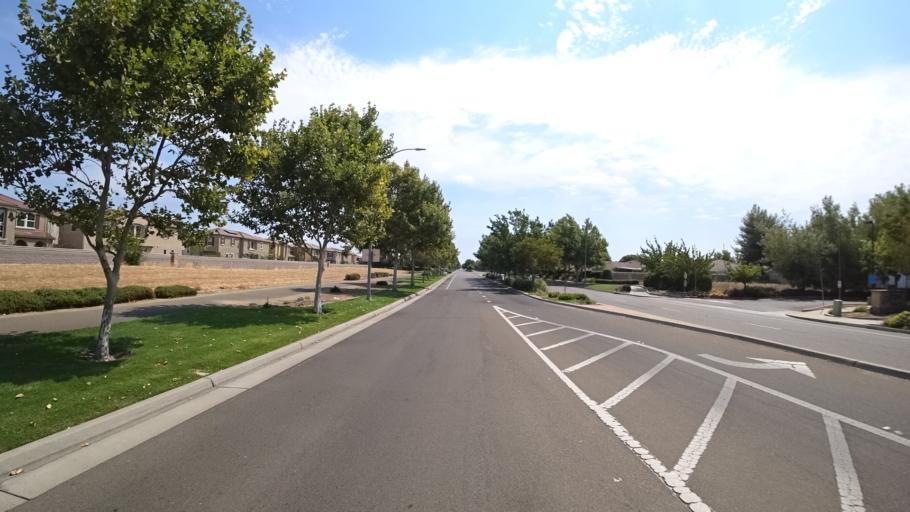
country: US
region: California
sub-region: Sacramento County
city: Laguna
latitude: 38.3937
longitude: -121.4510
